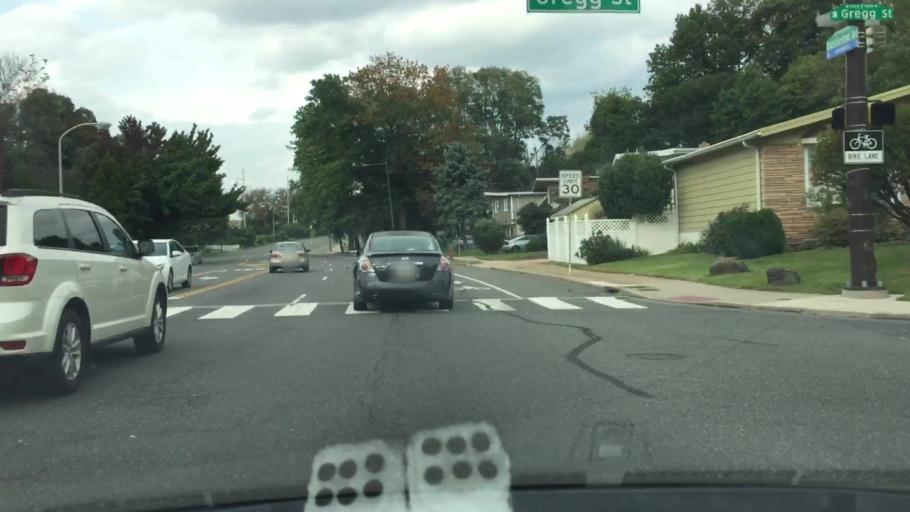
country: US
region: Pennsylvania
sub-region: Montgomery County
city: Rockledge
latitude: 40.0795
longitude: -75.0422
